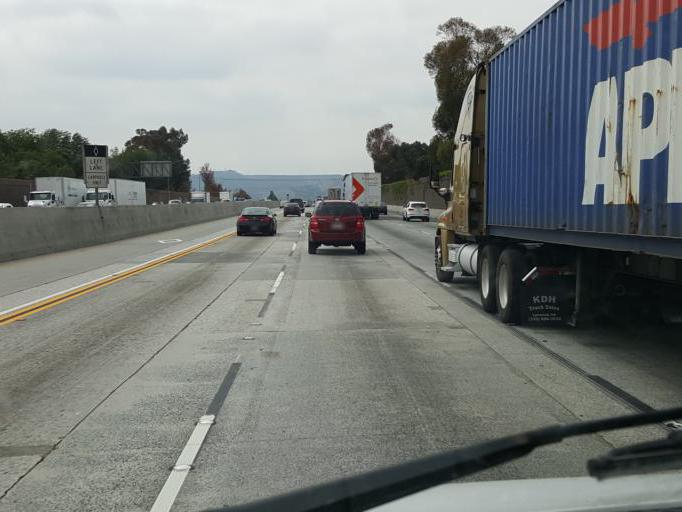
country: US
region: California
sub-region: Los Angeles County
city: La Puente
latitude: 34.0042
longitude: -117.9551
